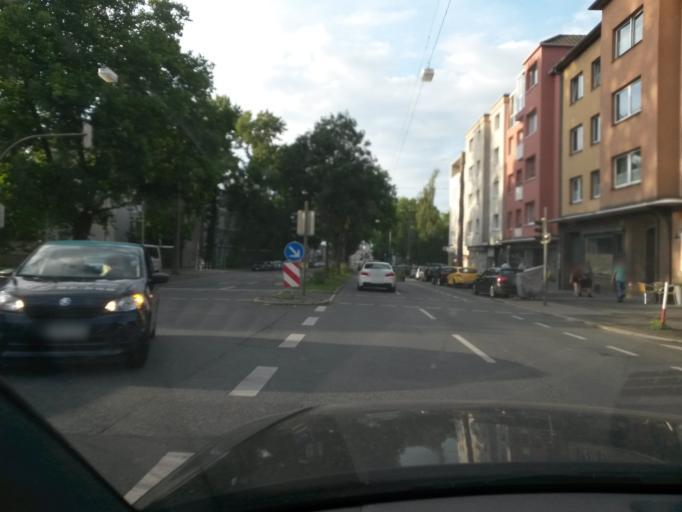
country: DE
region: North Rhine-Westphalia
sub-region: Regierungsbezirk Arnsberg
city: Dortmund
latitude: 51.5106
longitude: 7.4745
